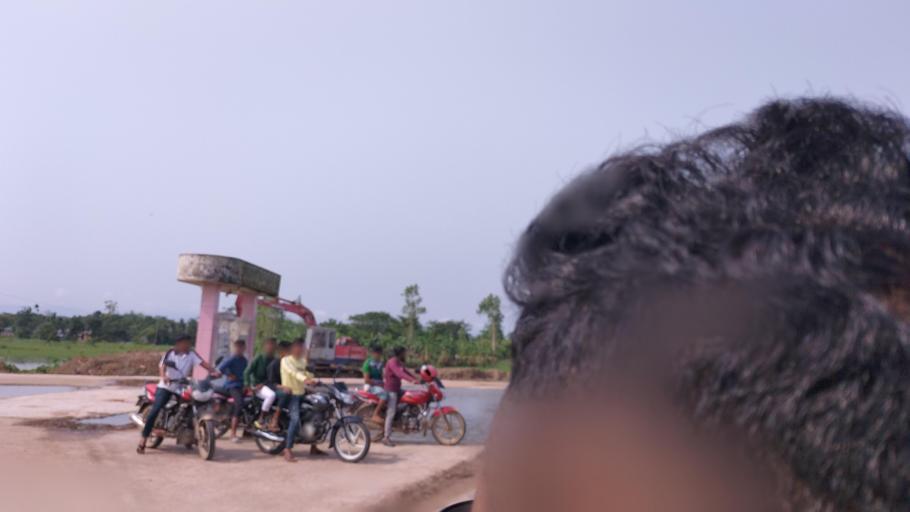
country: BD
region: Dhaka
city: Netrakona
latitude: 25.0693
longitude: 90.8841
